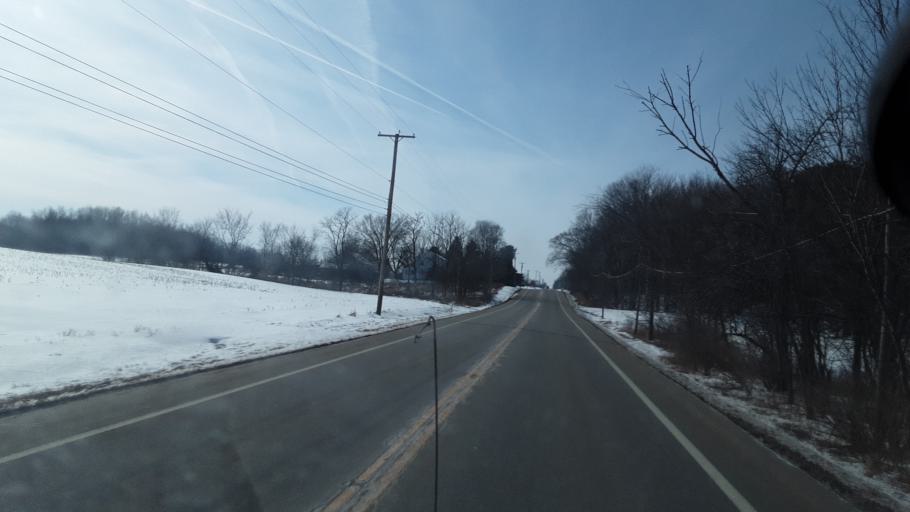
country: US
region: Ohio
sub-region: Mahoning County
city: Canfield
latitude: 41.0244
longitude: -80.8640
